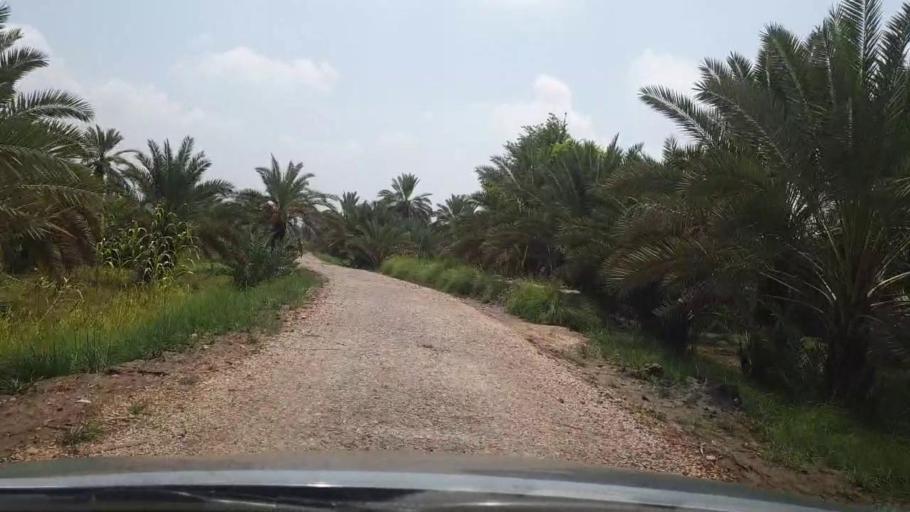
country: PK
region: Sindh
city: Pir jo Goth
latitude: 27.6190
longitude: 68.6571
